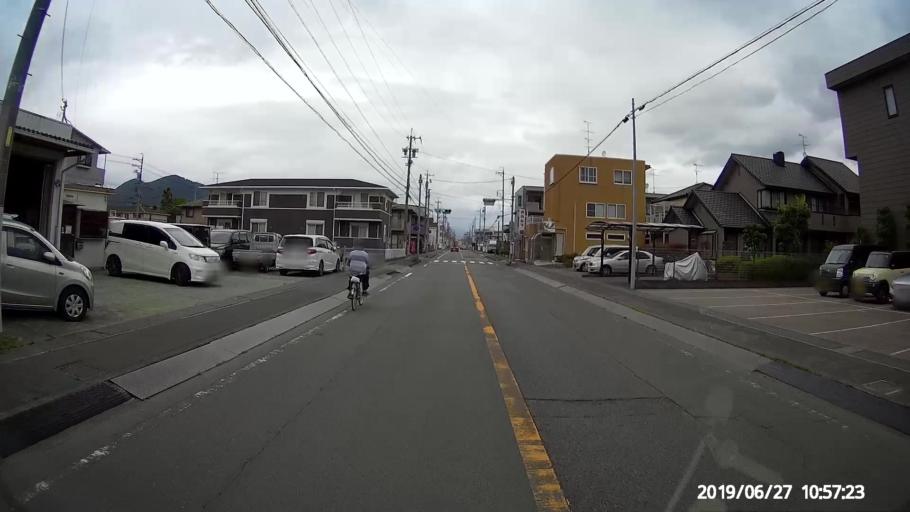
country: JP
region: Shizuoka
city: Shizuoka-shi
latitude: 34.9368
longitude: 138.3668
